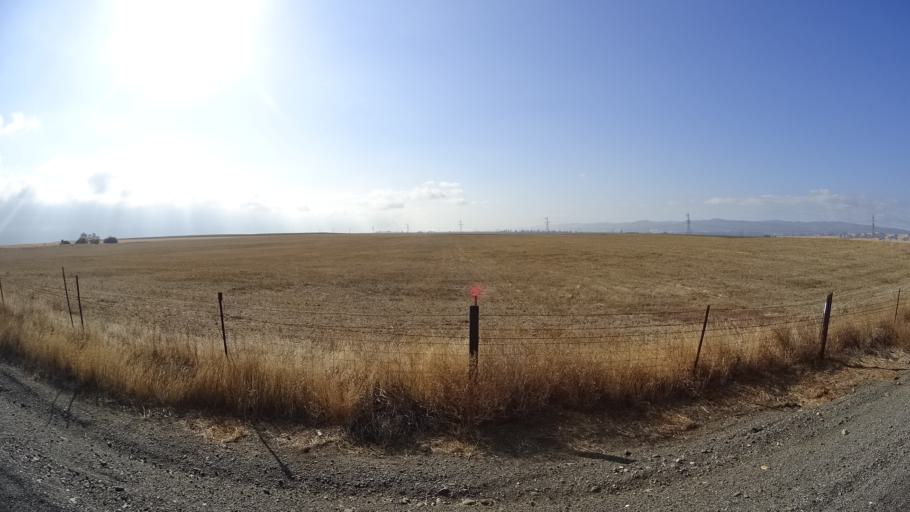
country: US
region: California
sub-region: Yolo County
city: Esparto
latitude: 38.7807
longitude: -121.9923
